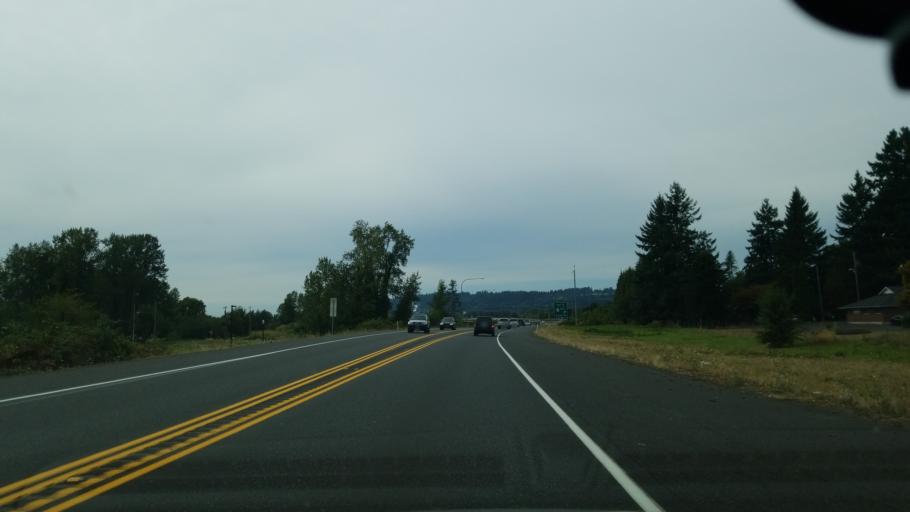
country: US
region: Washington
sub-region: Clark County
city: Washougal
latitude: 45.5787
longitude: -122.3670
